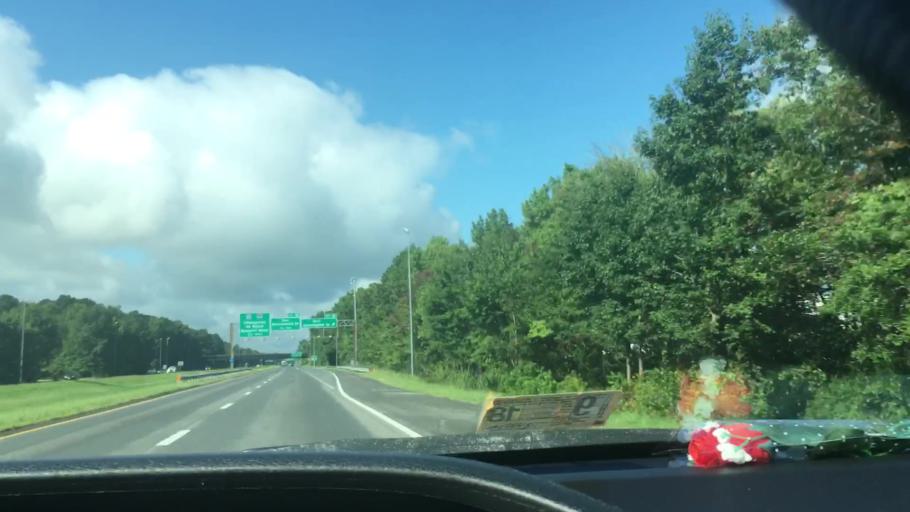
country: US
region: Virginia
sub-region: City of Portsmouth
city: Portsmouth Heights
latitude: 36.8024
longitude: -76.3725
